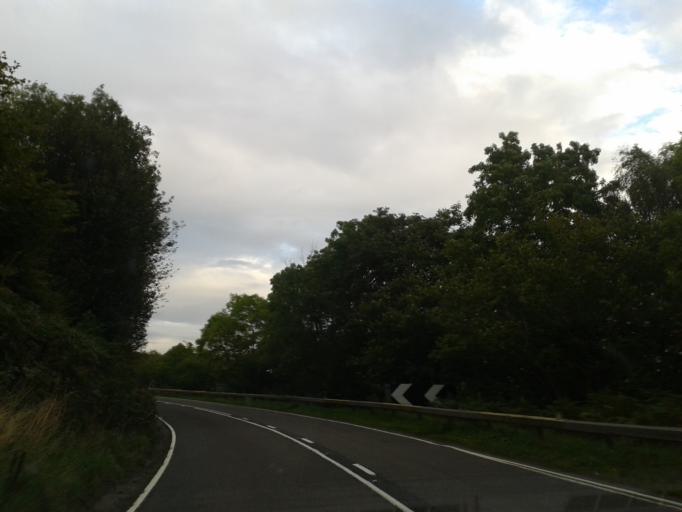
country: GB
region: Scotland
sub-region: Highland
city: Beauly
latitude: 57.3799
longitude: -4.3769
